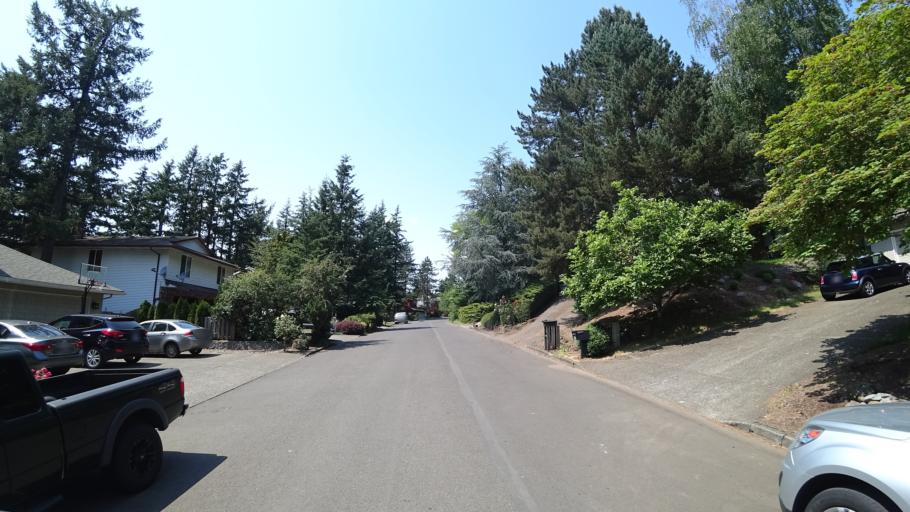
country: US
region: Oregon
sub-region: Clackamas County
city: Happy Valley
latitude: 45.4483
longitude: -122.5595
